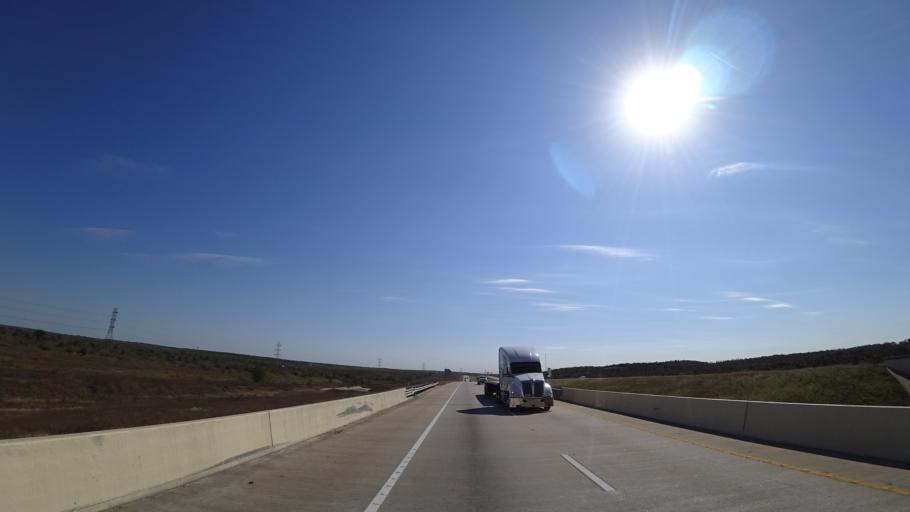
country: US
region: Texas
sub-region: Travis County
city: Manor
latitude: 30.3234
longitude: -97.5798
